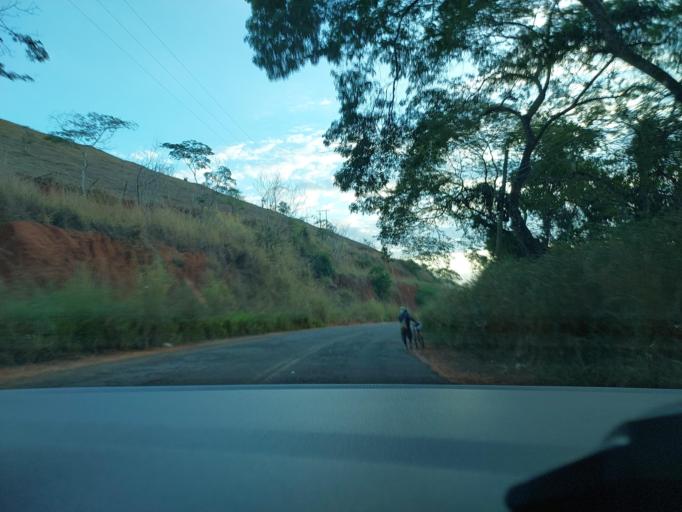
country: BR
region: Rio de Janeiro
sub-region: Natividade
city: Natividade
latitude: -21.1998
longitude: -42.1191
